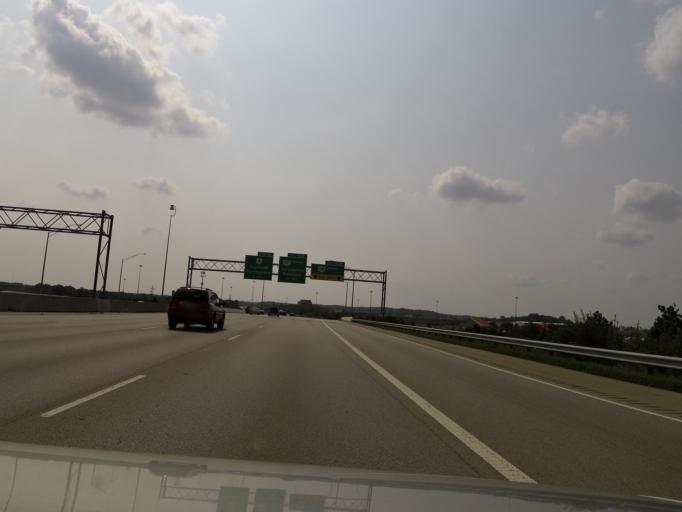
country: US
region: Ohio
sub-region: Hamilton County
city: Glendale
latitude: 39.2945
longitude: -84.4618
